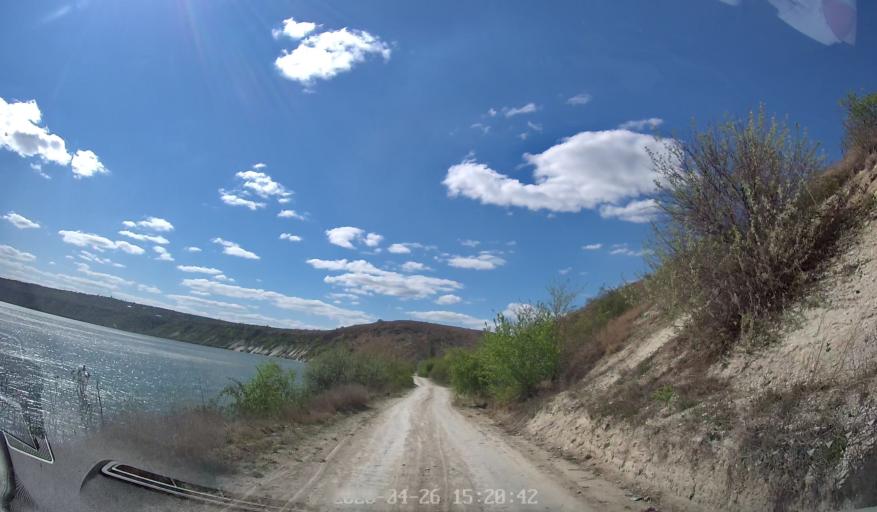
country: MD
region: Telenesti
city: Cocieri
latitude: 47.3640
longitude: 29.0958
